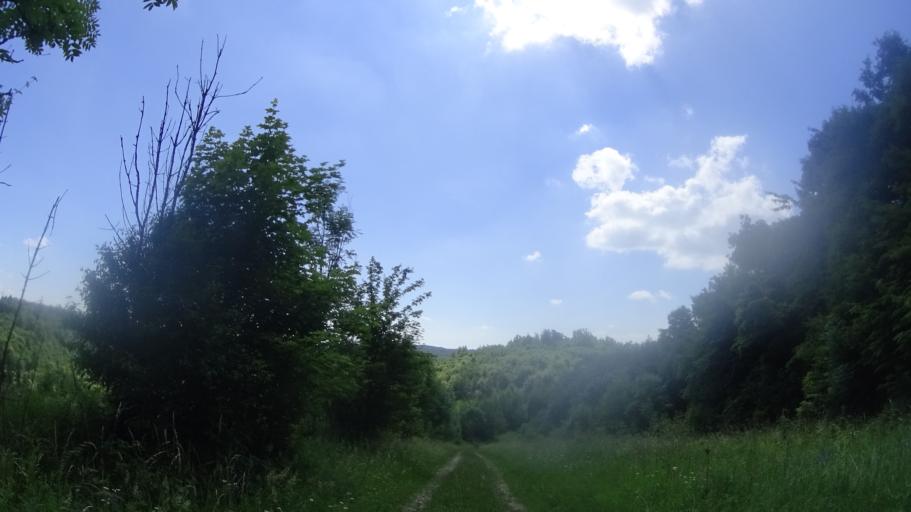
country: DE
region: Lower Saxony
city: Elbe
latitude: 52.1035
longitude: 10.3207
